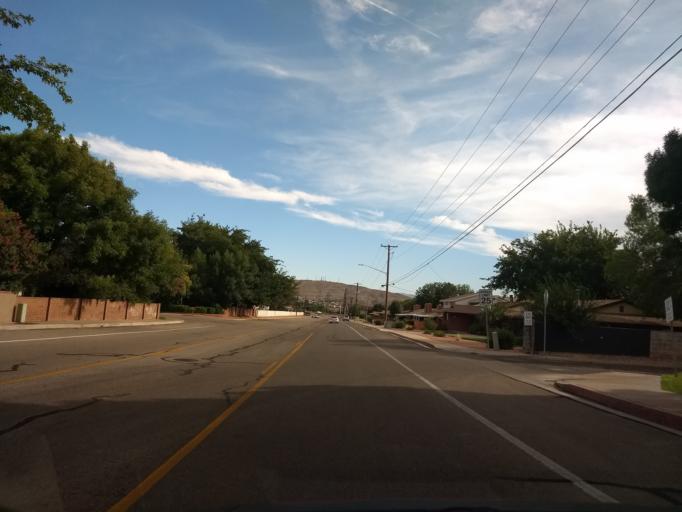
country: US
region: Utah
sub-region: Washington County
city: Saint George
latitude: 37.0944
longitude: -113.5750
